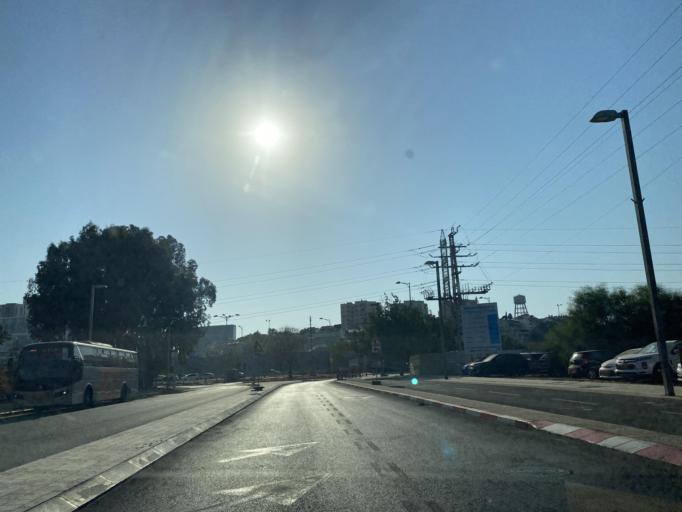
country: IL
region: Tel Aviv
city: Herzliyya
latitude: 32.1645
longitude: 34.8199
